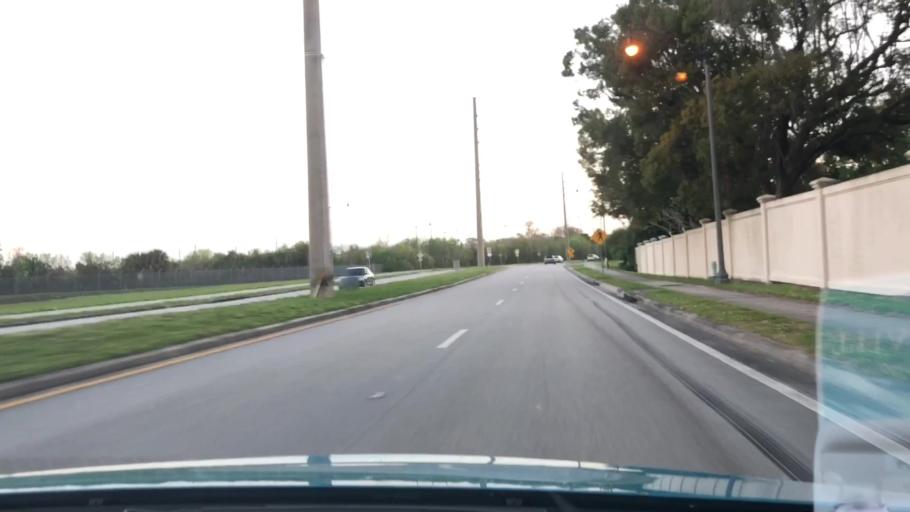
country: US
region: Florida
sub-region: Osceola County
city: Kissimmee
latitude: 28.2990
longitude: -81.3995
